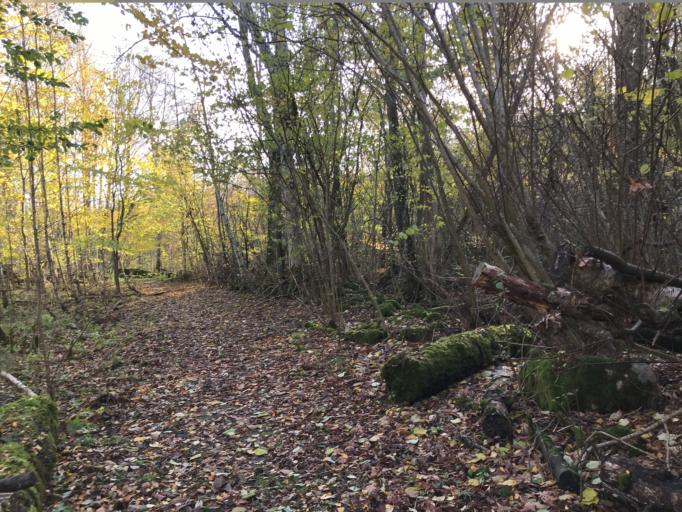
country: SE
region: Skane
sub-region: Svalovs Kommun
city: Kagerod
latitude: 56.0270
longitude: 13.1021
